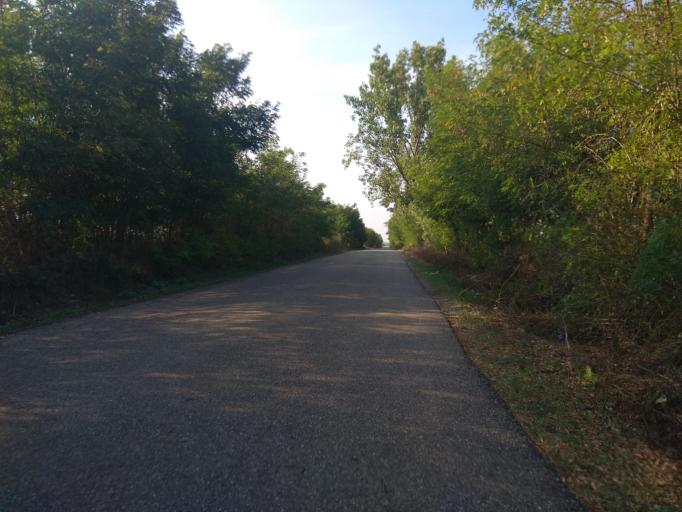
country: HU
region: Borsod-Abauj-Zemplen
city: Harsany
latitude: 47.9104
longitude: 20.7424
